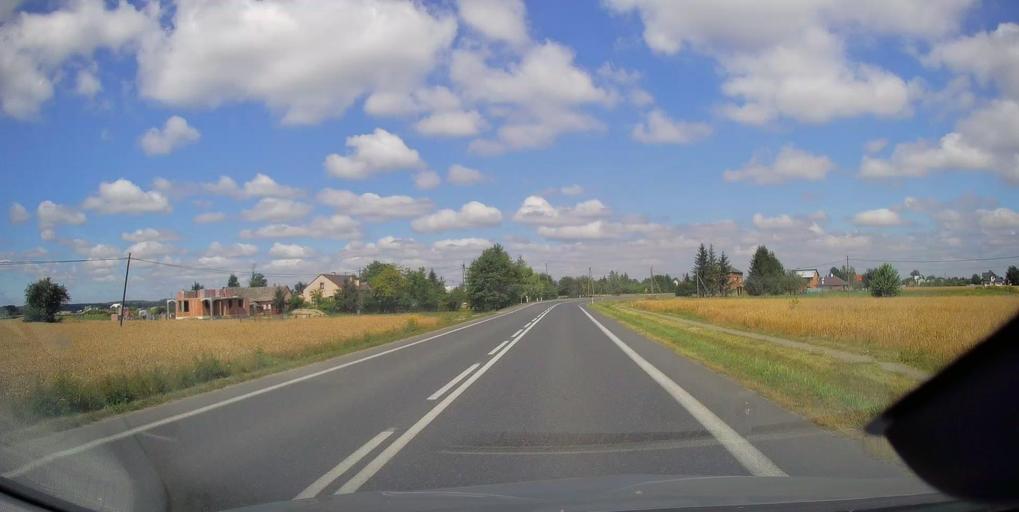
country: PL
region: Subcarpathian Voivodeship
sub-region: Powiat mielecki
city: Przeclaw
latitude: 50.1494
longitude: 21.4843
